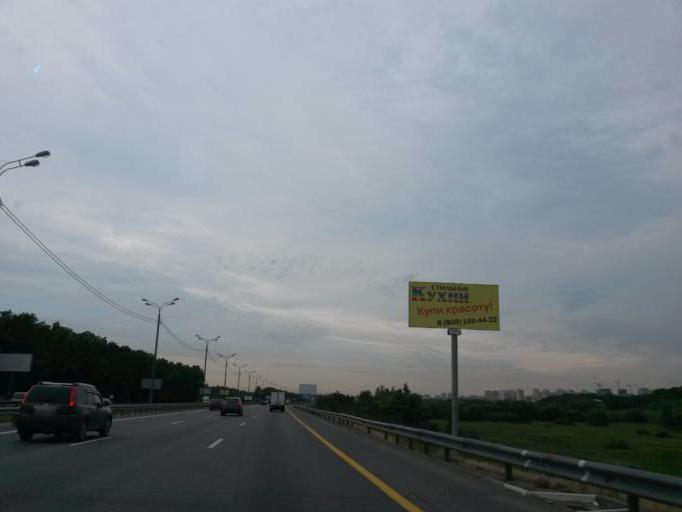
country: RU
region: Moskovskaya
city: Vidnoye
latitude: 55.5217
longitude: 37.7056
